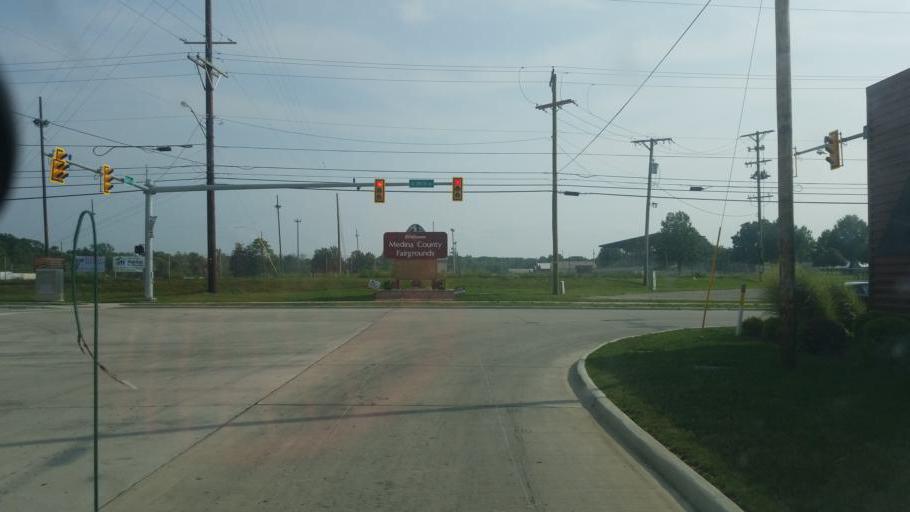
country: US
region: Ohio
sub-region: Medina County
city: Medina
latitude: 41.1365
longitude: -81.8784
